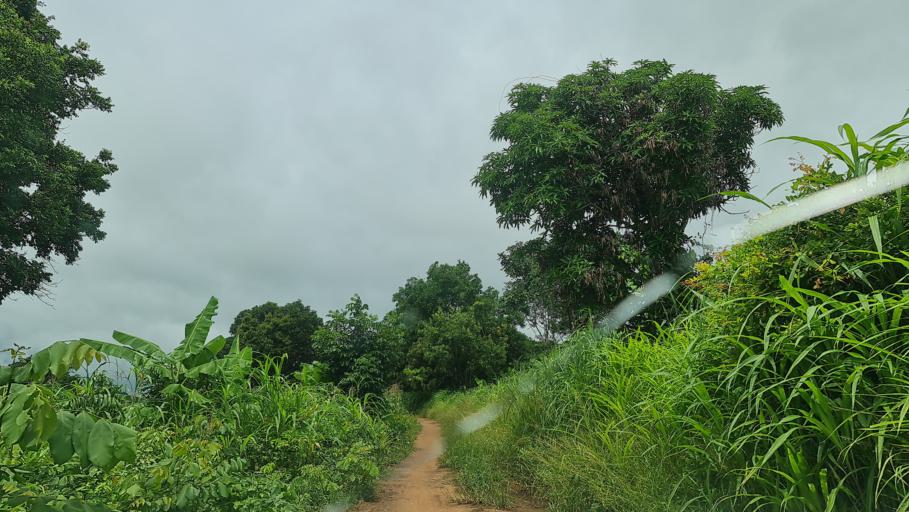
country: MW
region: Southern Region
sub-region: Nsanje District
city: Nsanje
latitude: -17.3834
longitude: 35.7778
